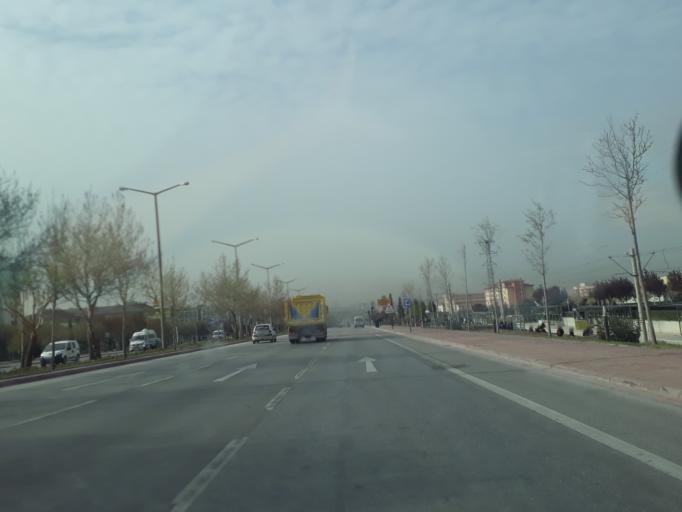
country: TR
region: Konya
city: Asagipinarbasi
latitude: 37.9901
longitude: 32.5182
